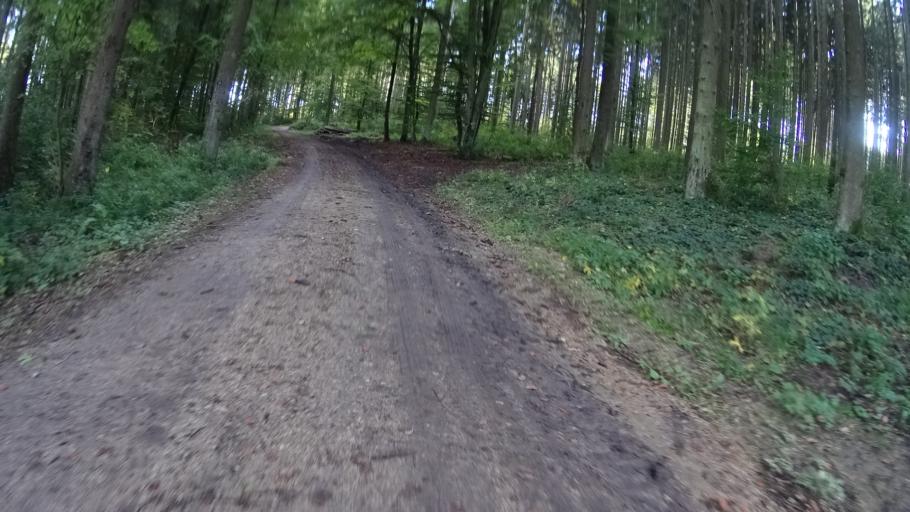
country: DE
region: Bavaria
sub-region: Upper Bavaria
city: Bohmfeld
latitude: 48.8766
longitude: 11.3572
